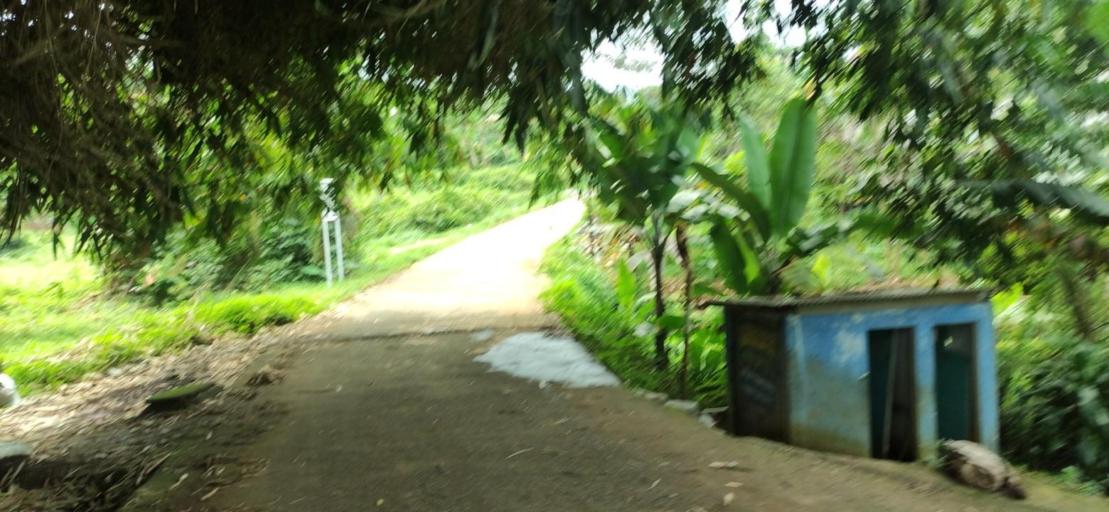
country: ID
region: West Java
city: Caringin
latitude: -6.6421
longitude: 106.8927
